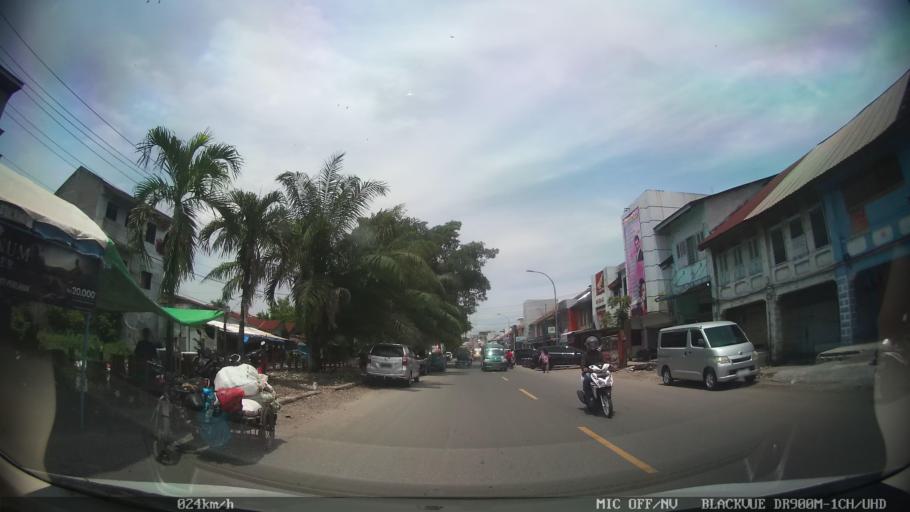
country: ID
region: North Sumatra
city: Belawan
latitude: 3.7827
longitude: 98.6859
